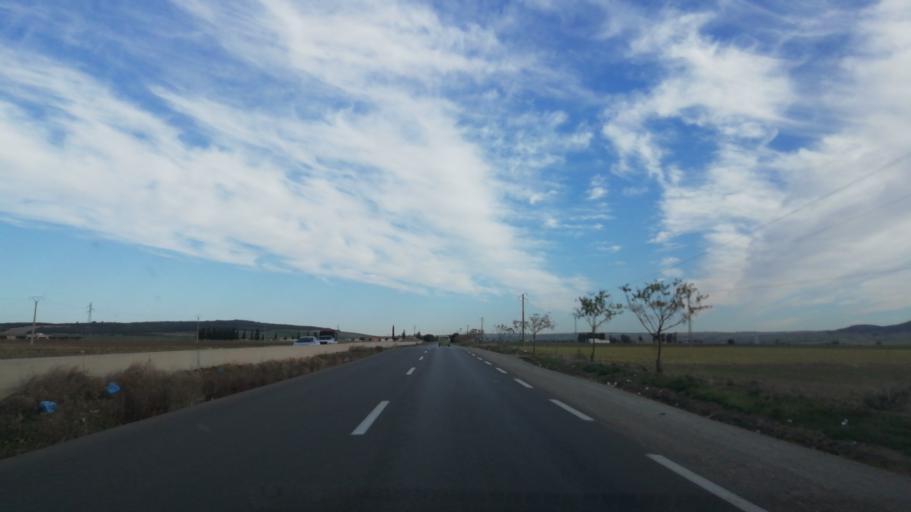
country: DZ
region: Sidi Bel Abbes
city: Sidi Bel Abbes
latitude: 35.1791
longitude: -0.4729
